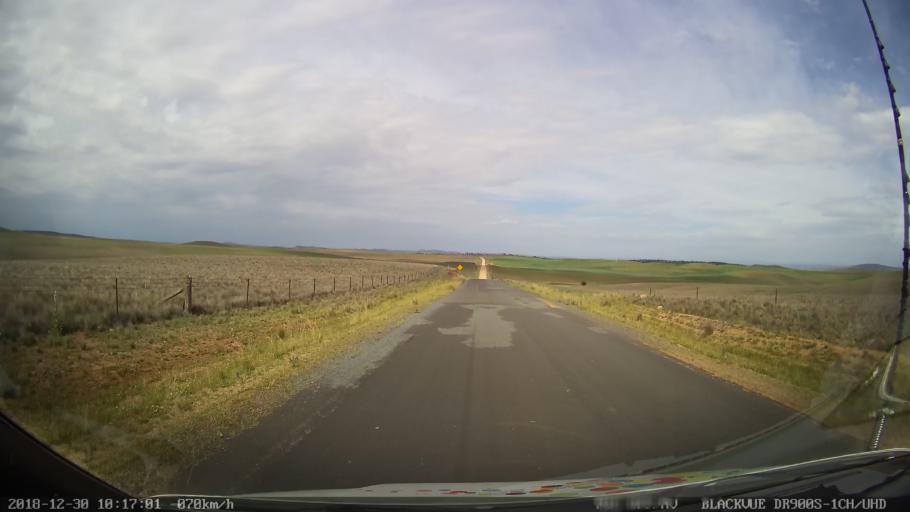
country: AU
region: New South Wales
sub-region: Snowy River
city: Berridale
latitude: -36.5472
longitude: 149.0265
